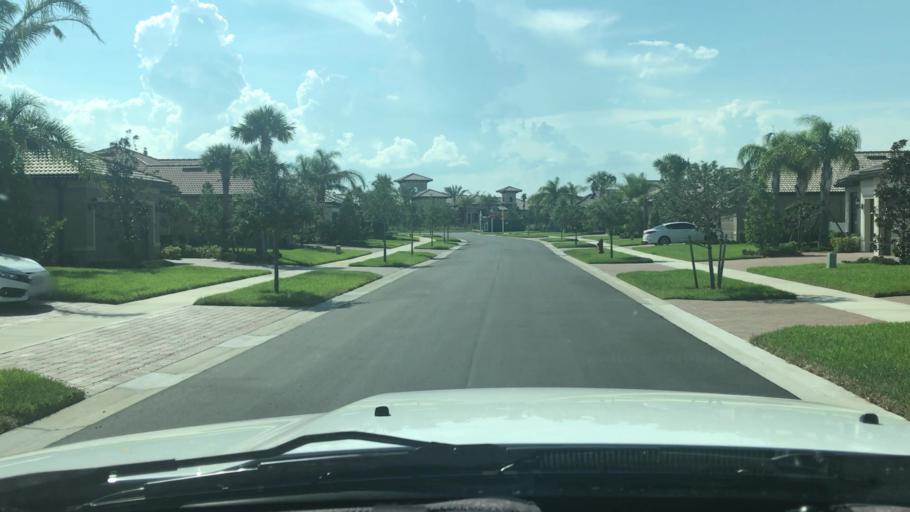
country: US
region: Florida
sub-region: Indian River County
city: Gifford
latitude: 27.6858
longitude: -80.4312
